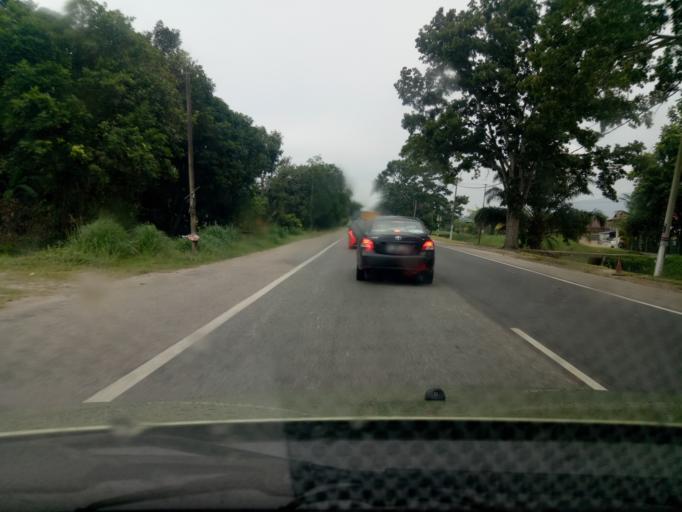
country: MY
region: Kedah
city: Gurun
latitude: 5.8813
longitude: 100.4467
